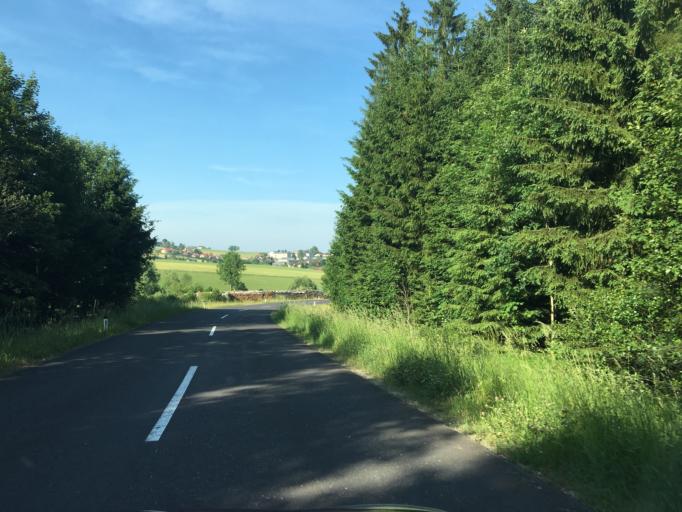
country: AT
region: Upper Austria
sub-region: Politischer Bezirk Urfahr-Umgebung
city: Bad Leonfelden
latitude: 48.5187
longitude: 14.2794
